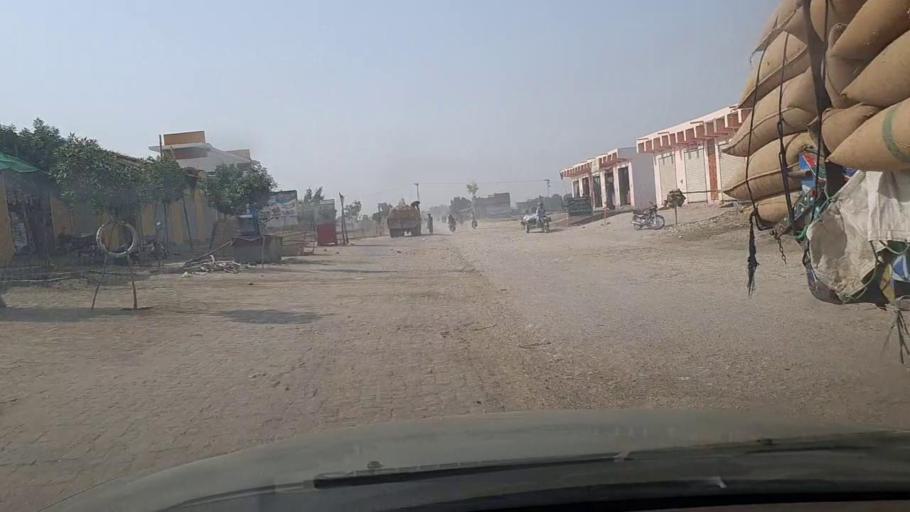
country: PK
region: Sindh
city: Mirpur Mathelo
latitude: 28.0119
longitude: 69.5474
